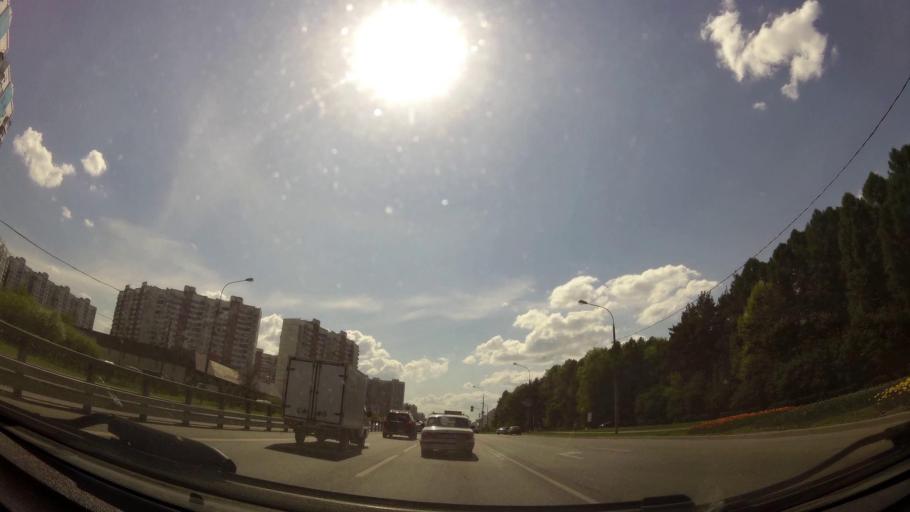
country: RU
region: Moscow
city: Solntsevo
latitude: 55.6461
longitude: 37.3662
